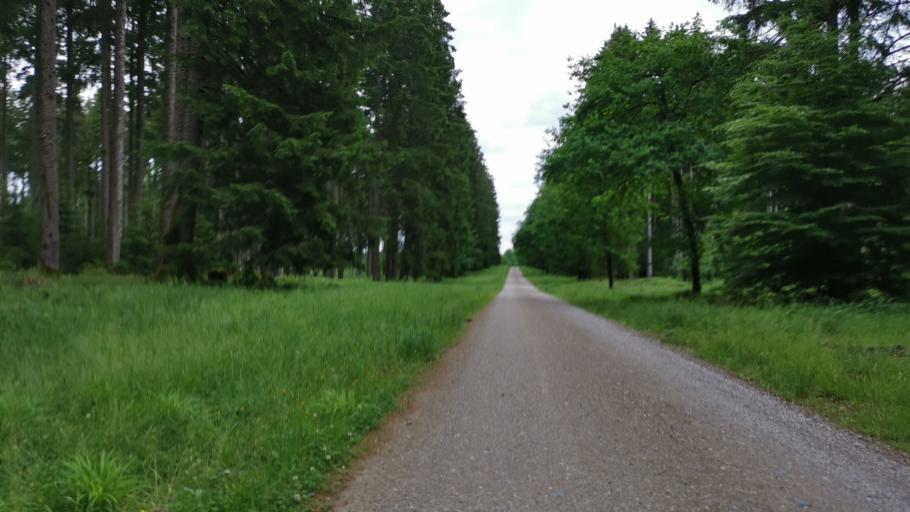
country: DE
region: Bavaria
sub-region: Upper Bavaria
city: Baierbrunn
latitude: 48.0351
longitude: 11.4596
